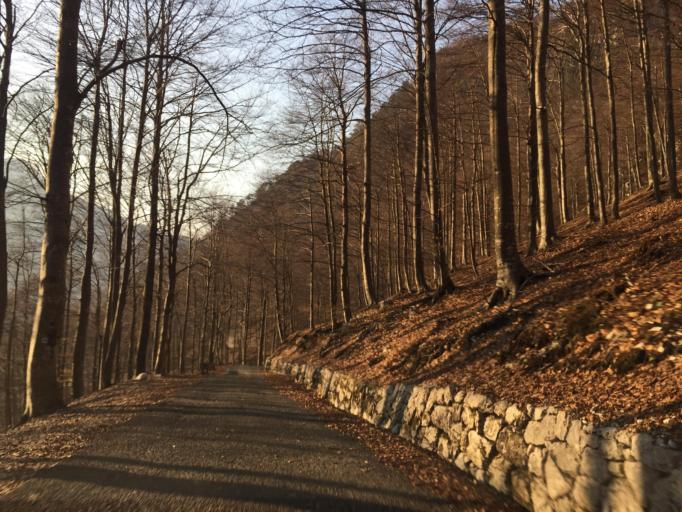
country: IT
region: Friuli Venezia Giulia
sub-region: Provincia di Udine
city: Prato
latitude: 46.3410
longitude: 13.3087
